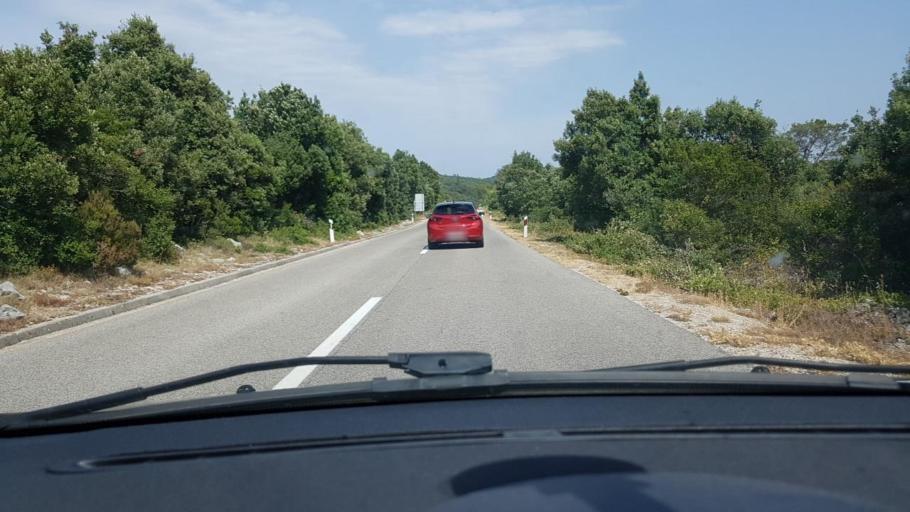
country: HR
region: Dubrovacko-Neretvanska
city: Smokvica
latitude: 42.9486
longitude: 16.9808
